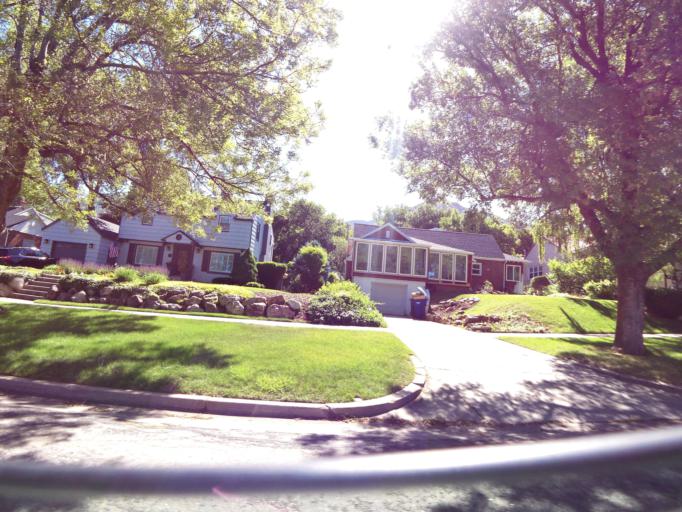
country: US
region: Utah
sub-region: Weber County
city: Ogden
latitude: 41.2123
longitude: -111.9429
